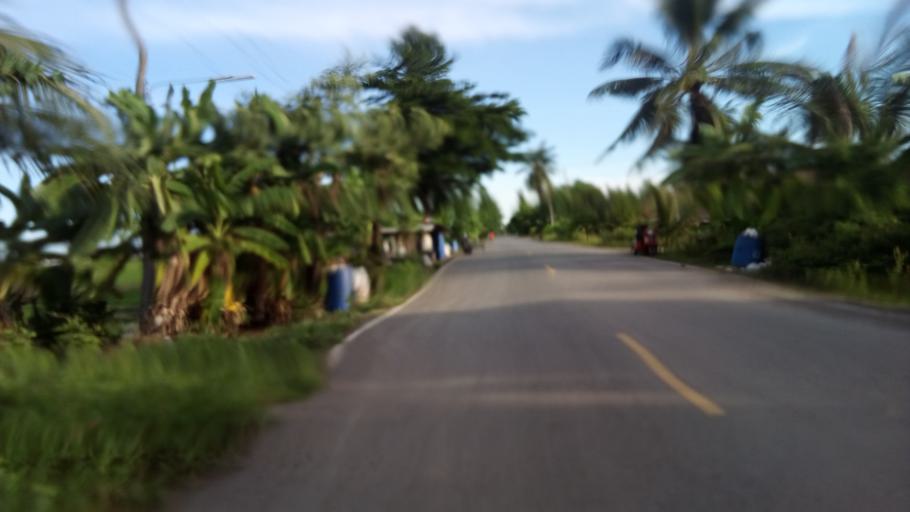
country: TH
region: Pathum Thani
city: Ban Lam Luk Ka
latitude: 14.0330
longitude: 100.8475
